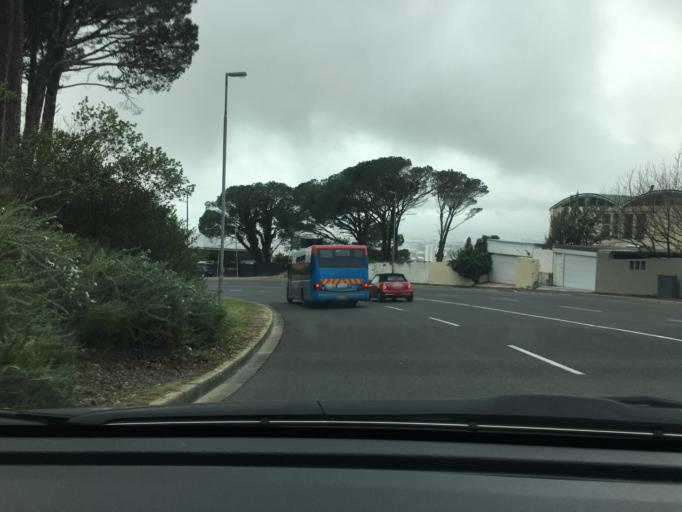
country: ZA
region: Western Cape
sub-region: City of Cape Town
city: Cape Town
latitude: -33.9391
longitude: 18.3975
